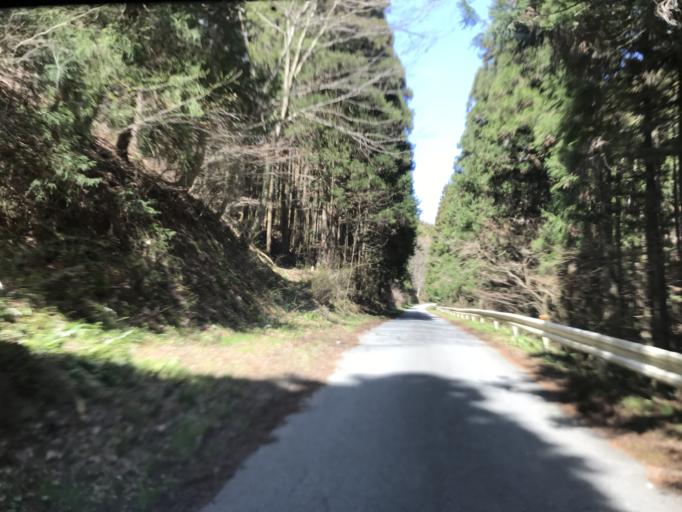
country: JP
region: Iwate
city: Ichinoseki
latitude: 38.8169
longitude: 141.2810
